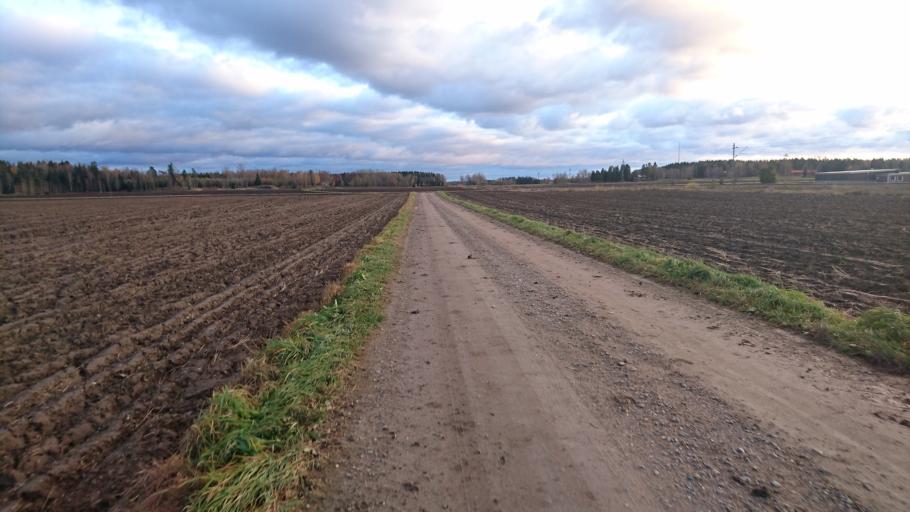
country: SE
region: Vaestmanland
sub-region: Sala Kommun
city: Sala
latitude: 59.8056
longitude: 16.6426
